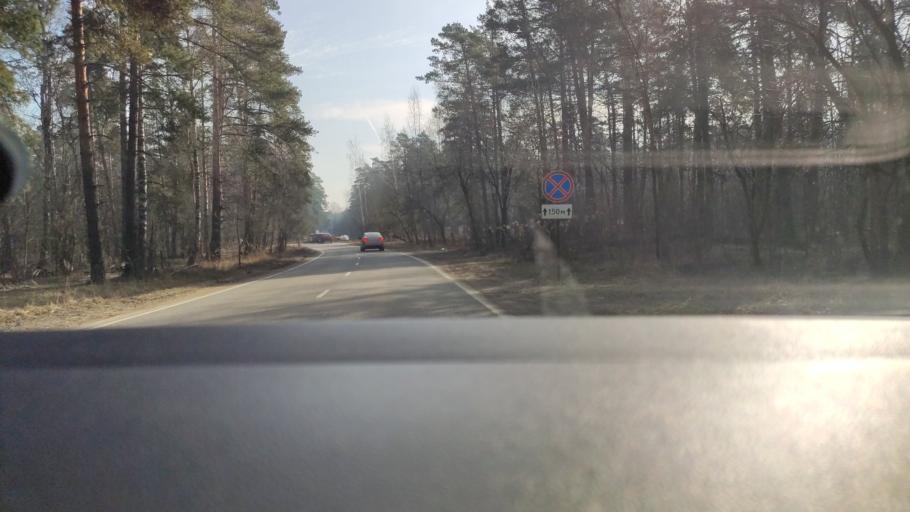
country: RU
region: Moskovskaya
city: Vishnyakovskiye Dachi
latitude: 55.8061
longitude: 38.1103
